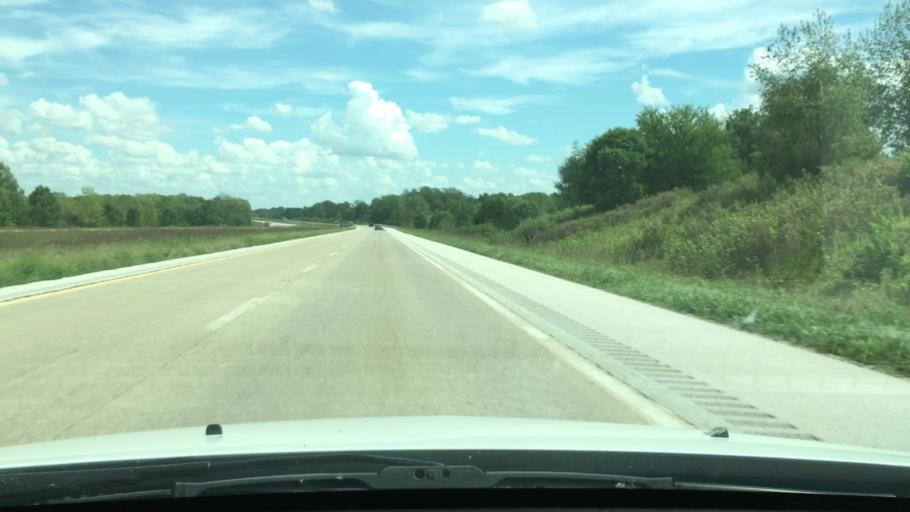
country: US
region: Illinois
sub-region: Scott County
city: Winchester
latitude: 39.6818
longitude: -90.5249
